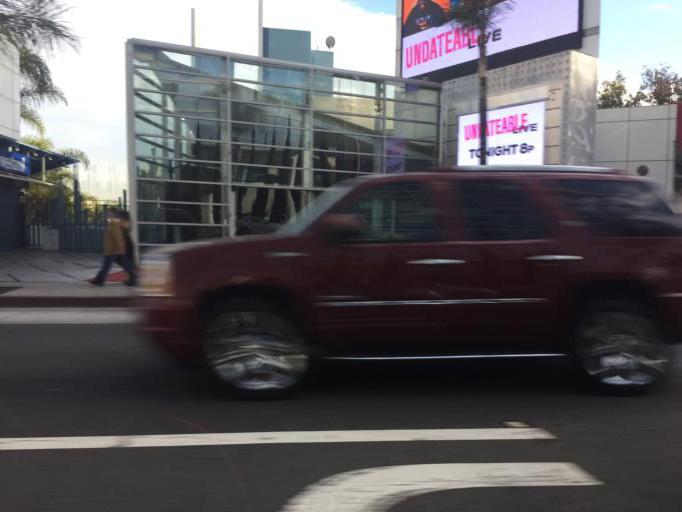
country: US
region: California
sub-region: Los Angeles County
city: West Hollywood
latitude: 34.0952
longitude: -118.3731
